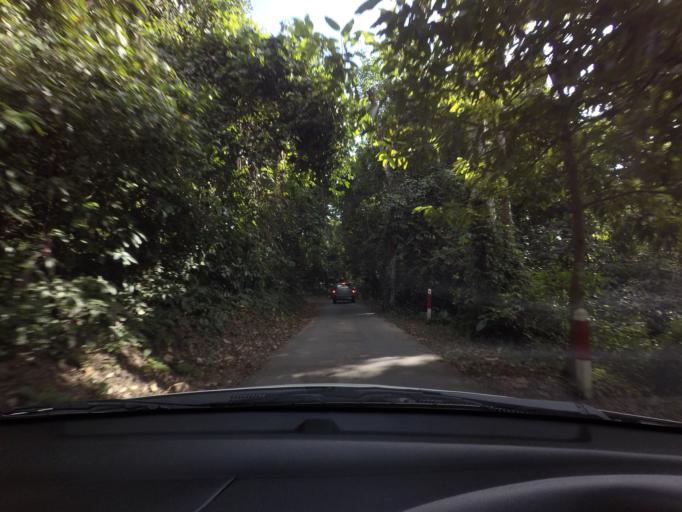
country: TH
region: Nakhon Nayok
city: Nakhon Nayok
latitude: 14.3254
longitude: 101.3076
